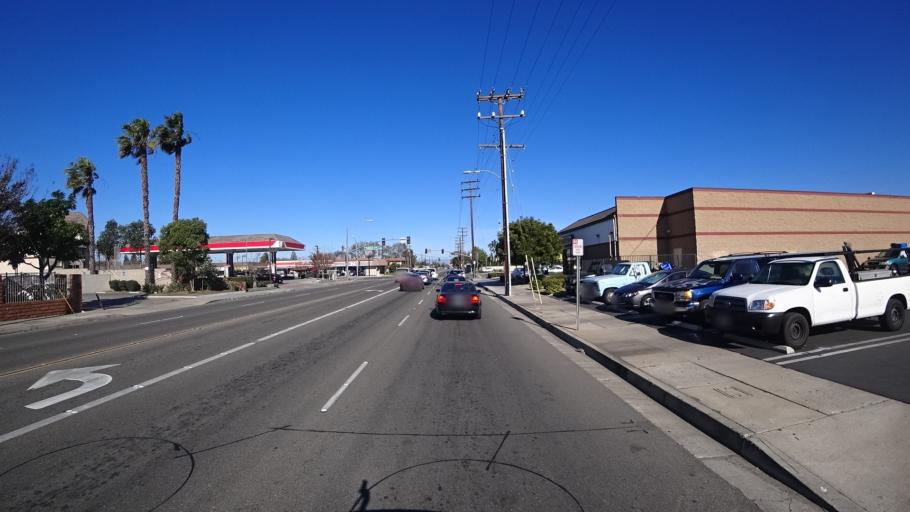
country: US
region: California
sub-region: Orange County
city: Midway City
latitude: 33.7586
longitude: -117.9810
